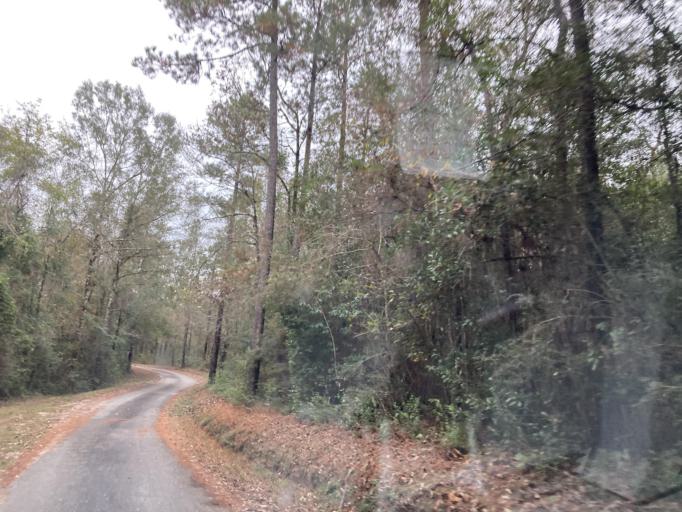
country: US
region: Mississippi
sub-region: Lamar County
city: Purvis
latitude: 31.1951
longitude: -89.4476
